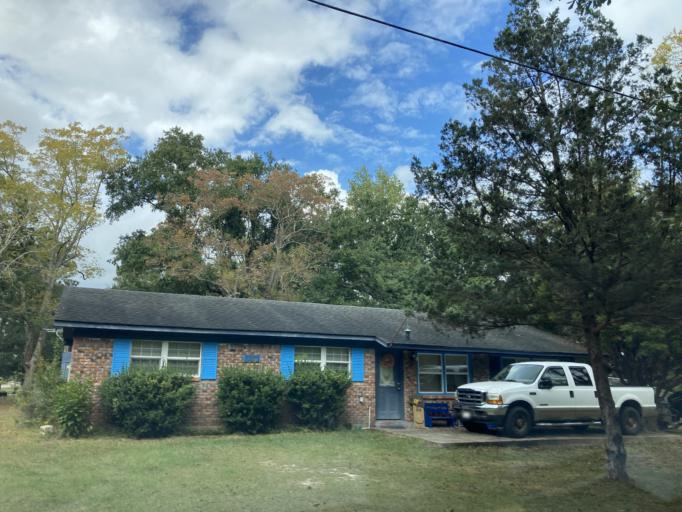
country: US
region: Mississippi
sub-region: Jackson County
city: Gulf Hills
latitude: 30.4334
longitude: -88.8322
